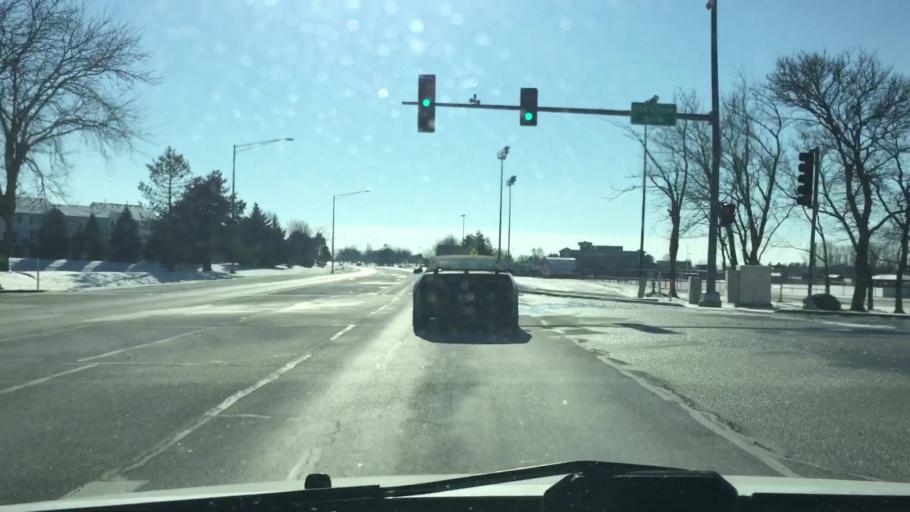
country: US
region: Illinois
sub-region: Kane County
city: Saint Charles
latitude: 41.9302
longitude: -88.2761
